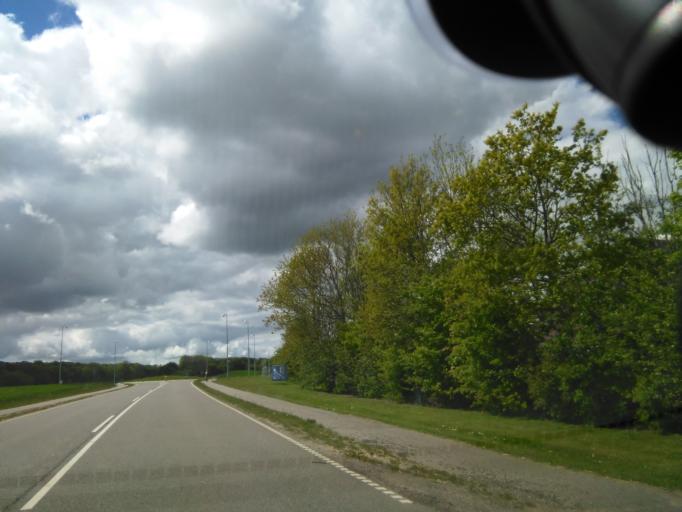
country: DK
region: Central Jutland
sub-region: Skanderborg Kommune
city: Horning
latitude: 56.0734
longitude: 10.0305
